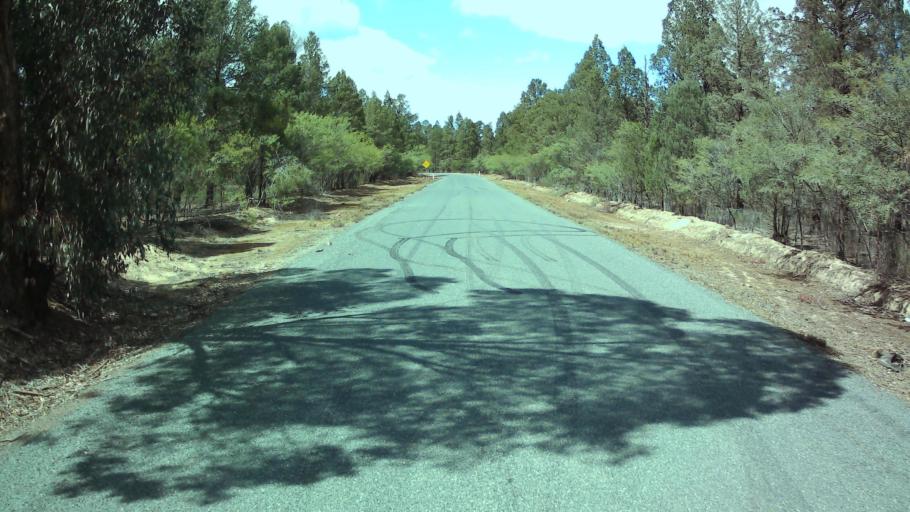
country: AU
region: New South Wales
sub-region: Weddin
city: Grenfell
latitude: -33.9078
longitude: 147.9195
